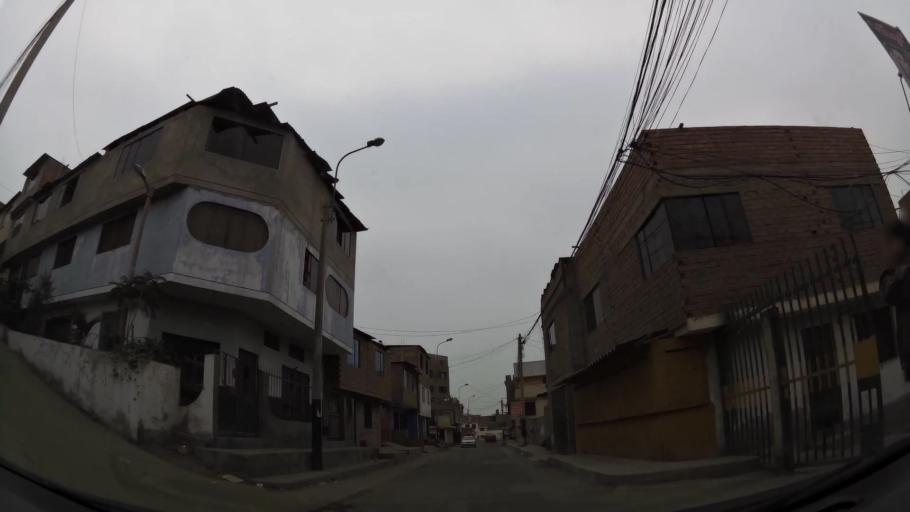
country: PE
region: Lima
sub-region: Lima
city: Surco
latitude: -12.1907
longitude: -76.9786
